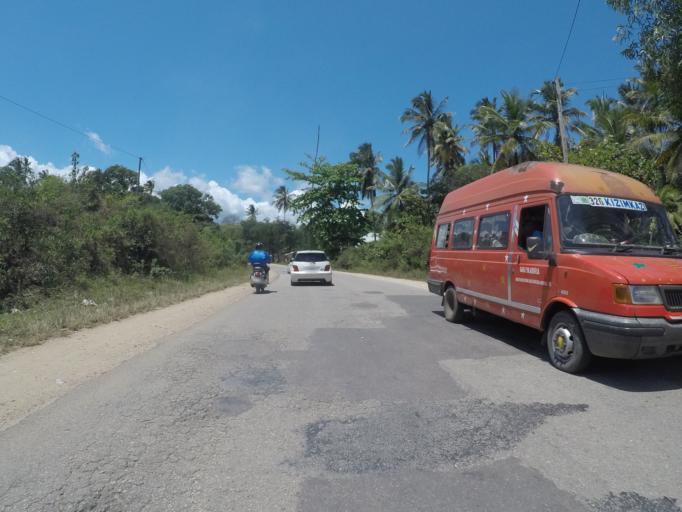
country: TZ
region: Zanzibar Central/South
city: Koani
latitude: -6.2015
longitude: 39.3159
